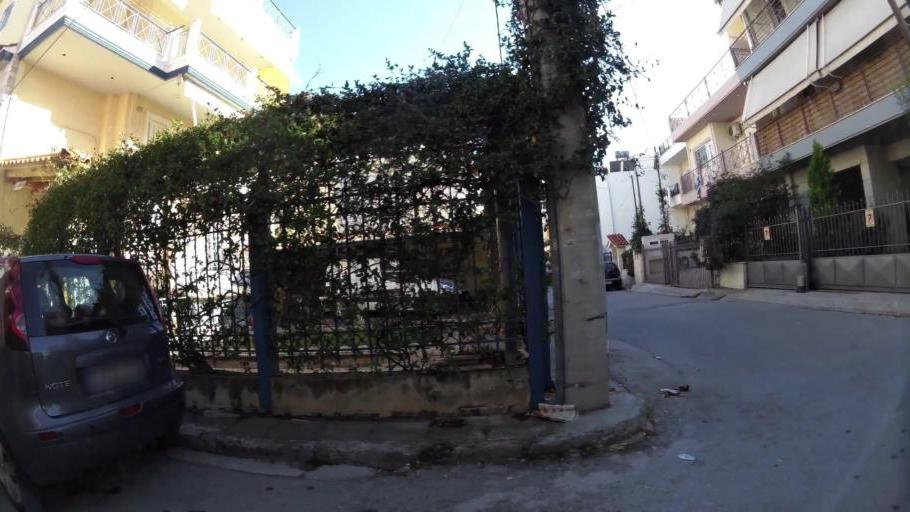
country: GR
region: Attica
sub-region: Nomarchia Anatolikis Attikis
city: Acharnes
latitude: 38.0871
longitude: 23.7300
